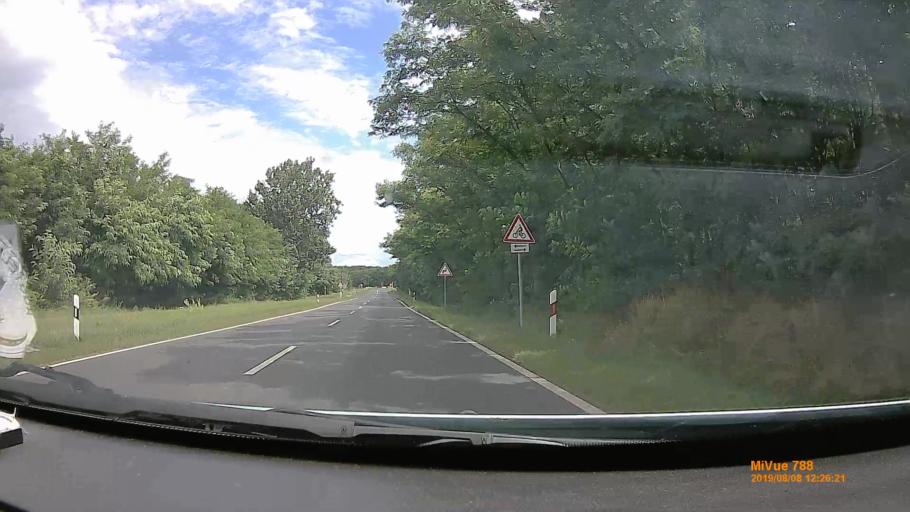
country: HU
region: Szabolcs-Szatmar-Bereg
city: Nyirbogat
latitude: 47.8168
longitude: 22.0874
